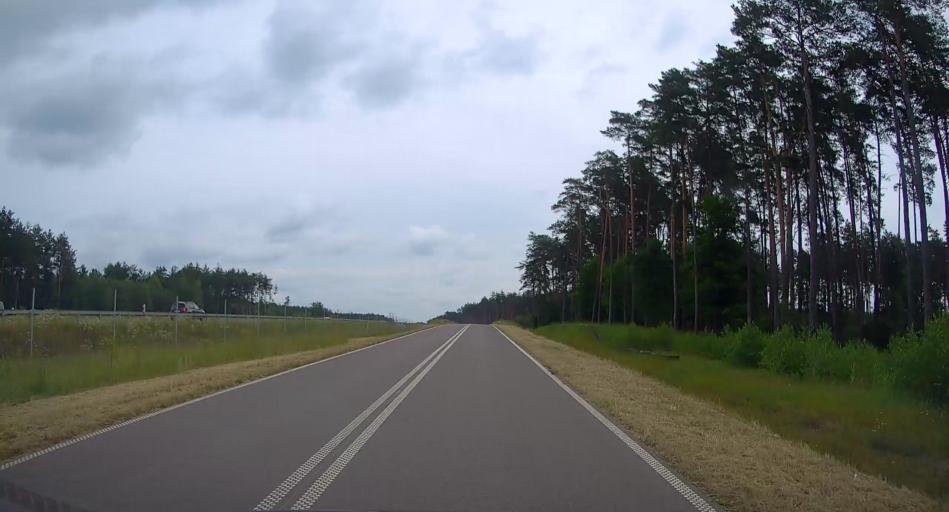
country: PL
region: Masovian Voivodeship
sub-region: Powiat ostrowski
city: Brok
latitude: 52.7259
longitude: 21.7252
